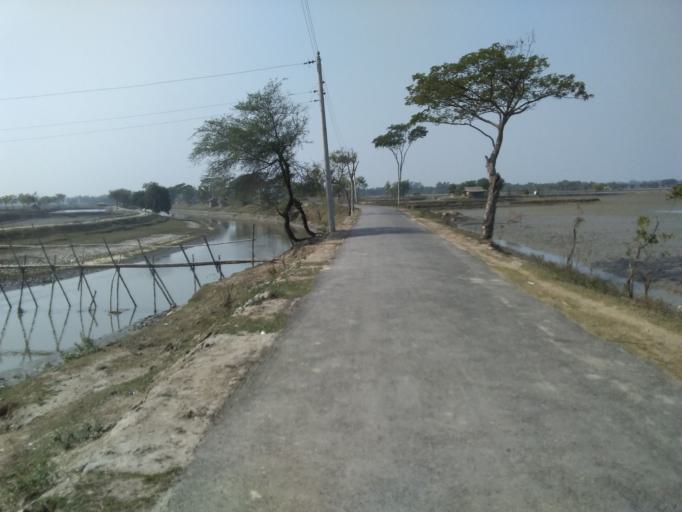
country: IN
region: West Bengal
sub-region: North 24 Parganas
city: Taki
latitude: 22.6350
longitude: 89.0084
